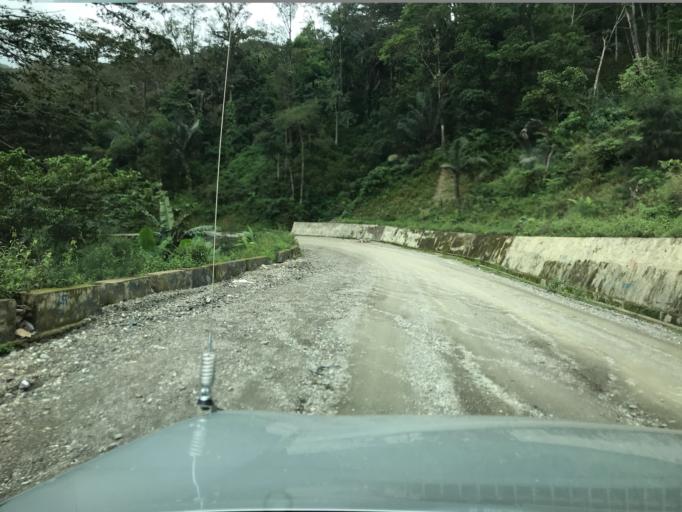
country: TL
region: Aileu
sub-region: Aileu Villa
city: Aileu
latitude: -8.6724
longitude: 125.5517
